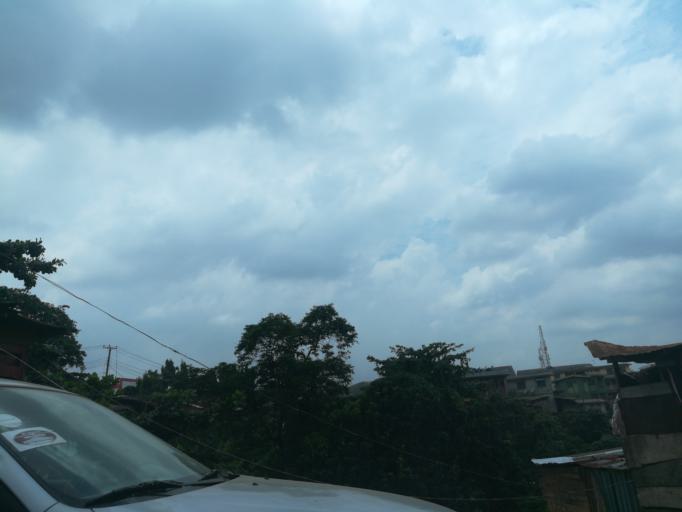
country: NG
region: Lagos
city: Ojota
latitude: 6.5886
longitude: 3.3744
